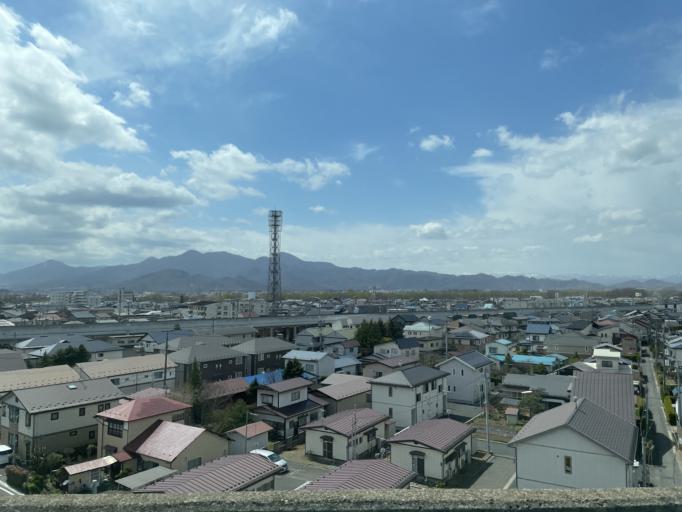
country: JP
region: Iwate
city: Morioka-shi
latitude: 39.7094
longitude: 141.1275
